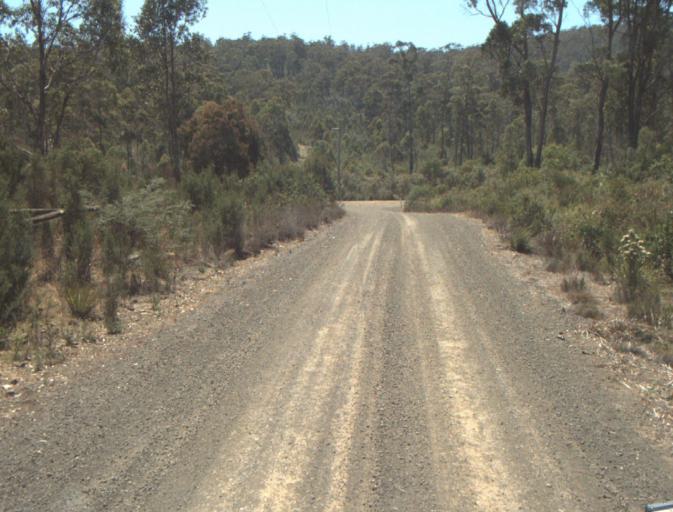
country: AU
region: Tasmania
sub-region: Launceston
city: Mayfield
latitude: -41.2729
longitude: 147.0995
